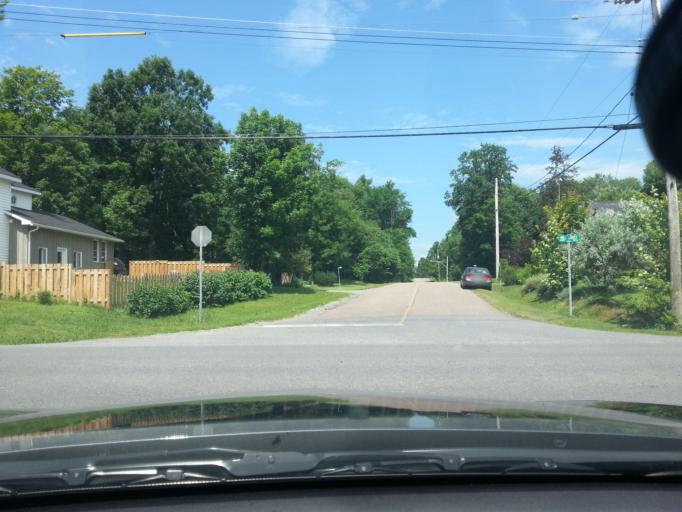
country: CA
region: Ontario
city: Renfrew
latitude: 45.2974
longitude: -76.7268
